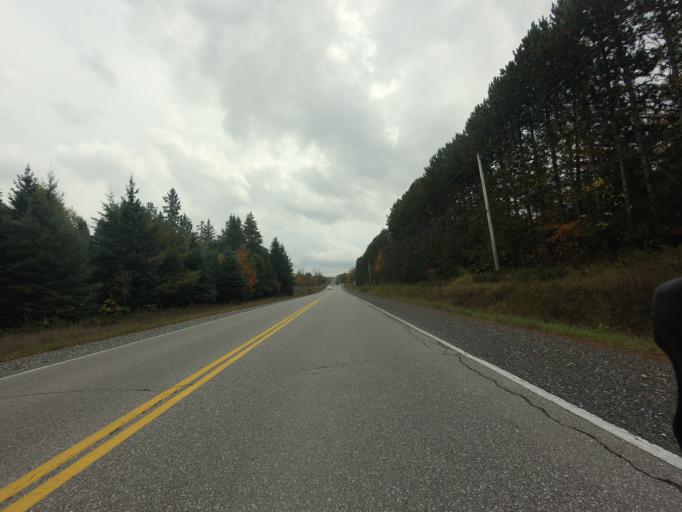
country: CA
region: Ontario
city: Perth
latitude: 45.0960
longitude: -76.4632
